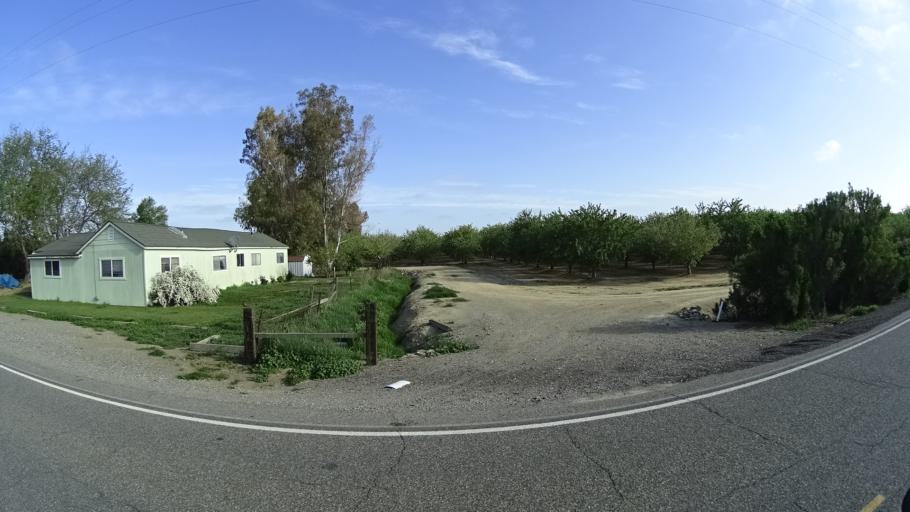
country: US
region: California
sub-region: Glenn County
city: Willows
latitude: 39.5822
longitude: -122.1556
